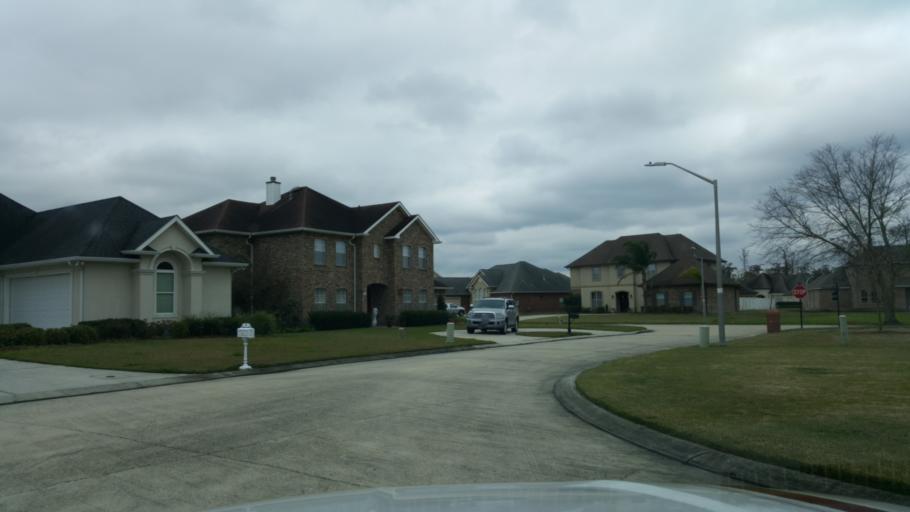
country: US
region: Louisiana
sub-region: Jefferson Parish
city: Woodmere
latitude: 29.8773
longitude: -90.0772
